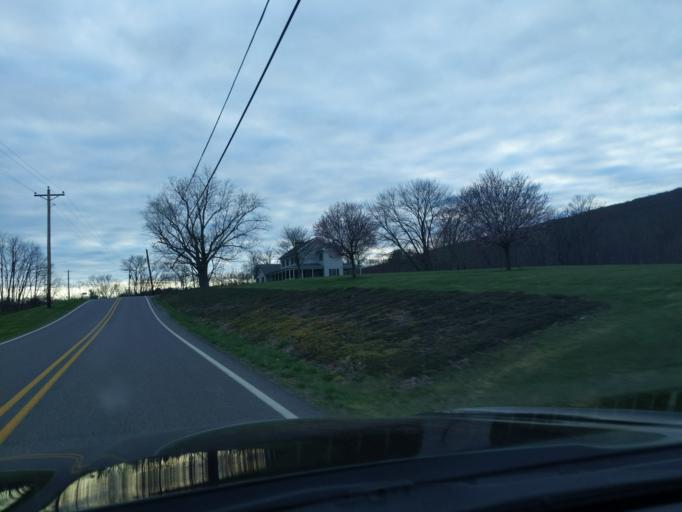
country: US
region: Pennsylvania
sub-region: Blair County
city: Lakemont
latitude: 40.4647
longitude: -78.3436
